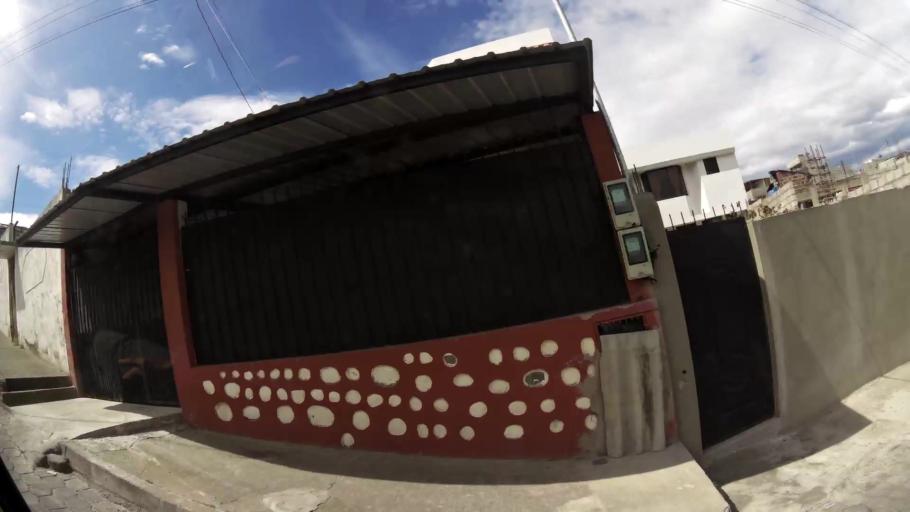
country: EC
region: Cotopaxi
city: Latacunga
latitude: -0.9344
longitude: -78.6076
